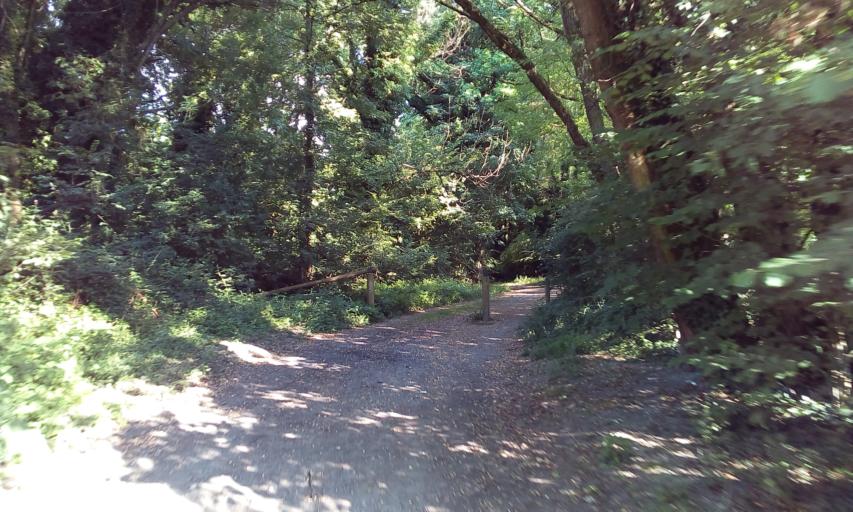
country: FR
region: Rhone-Alpes
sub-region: Departement de l'Isere
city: Gieres
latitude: 45.1931
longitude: 5.7944
